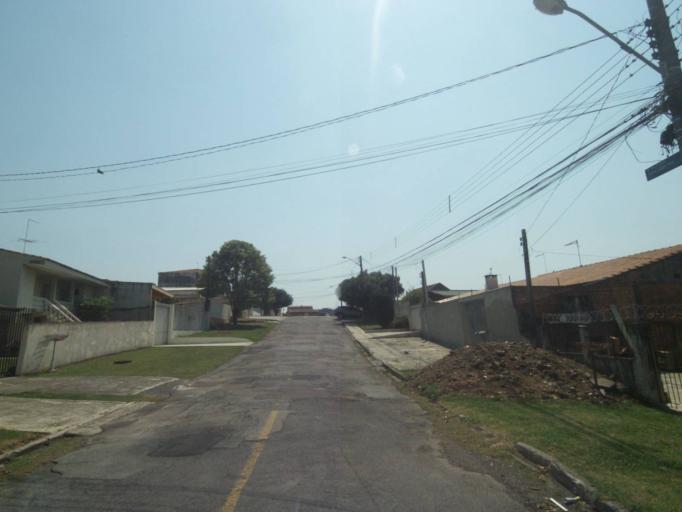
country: BR
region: Parana
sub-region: Sao Jose Dos Pinhais
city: Sao Jose dos Pinhais
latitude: -25.5061
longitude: -49.2693
